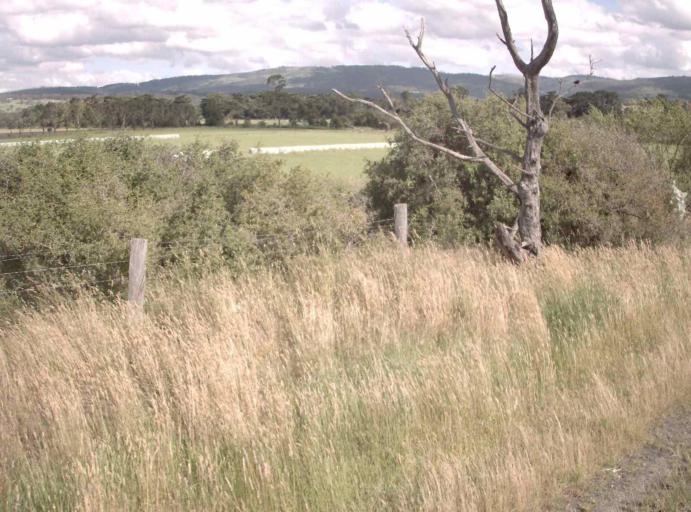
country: AU
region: Victoria
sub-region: Latrobe
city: Morwell
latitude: -38.2869
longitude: 146.4304
